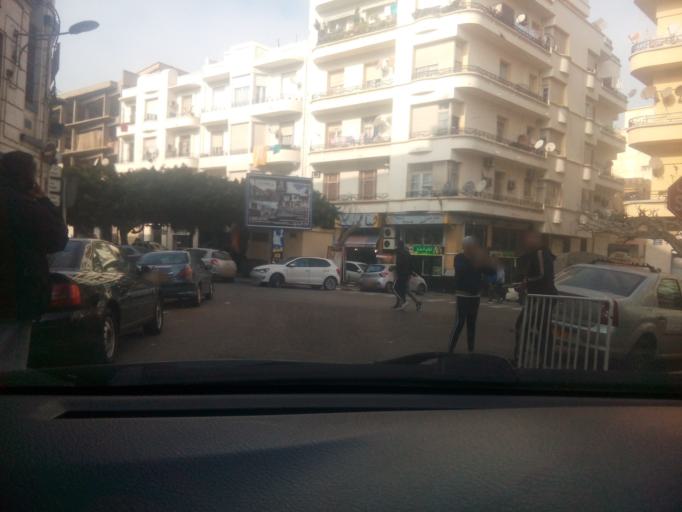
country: DZ
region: Oran
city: Oran
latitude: 35.7034
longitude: -0.6410
